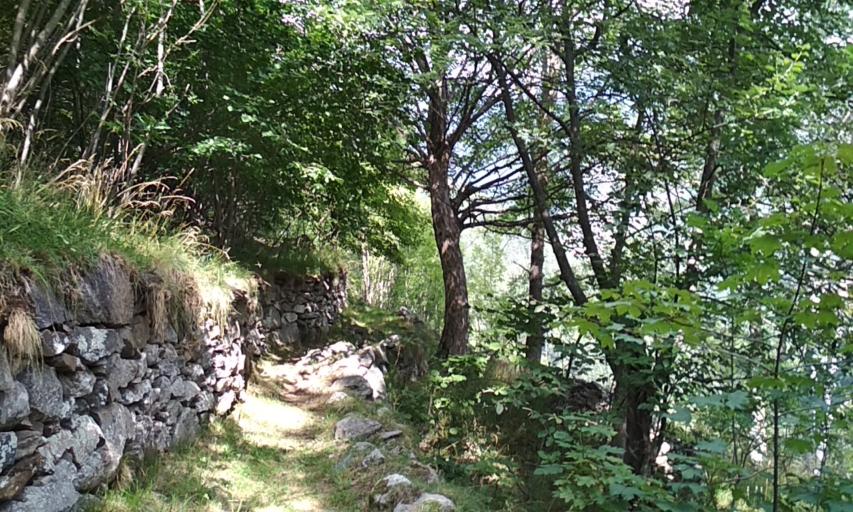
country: IT
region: Piedmont
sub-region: Provincia di Torino
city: Noasca
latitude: 45.4595
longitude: 7.3021
